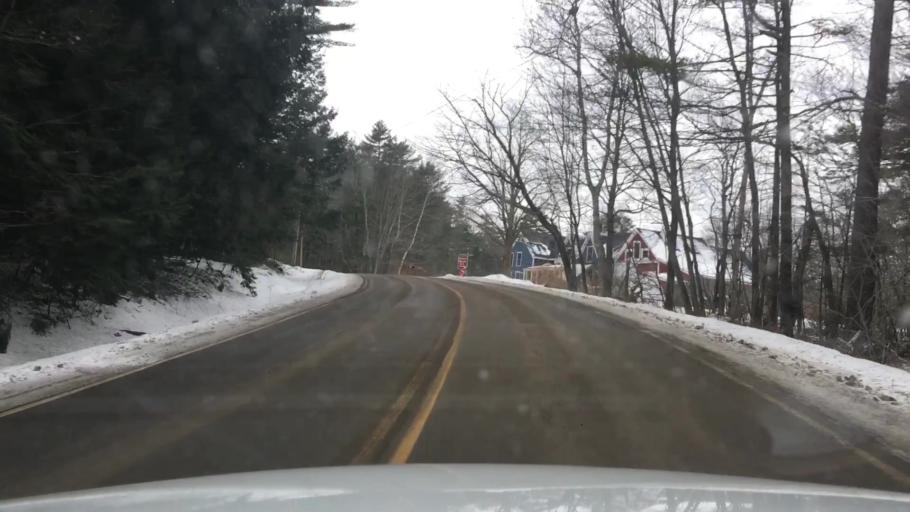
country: US
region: Maine
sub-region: Waldo County
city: Lincolnville
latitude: 44.2894
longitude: -69.0240
